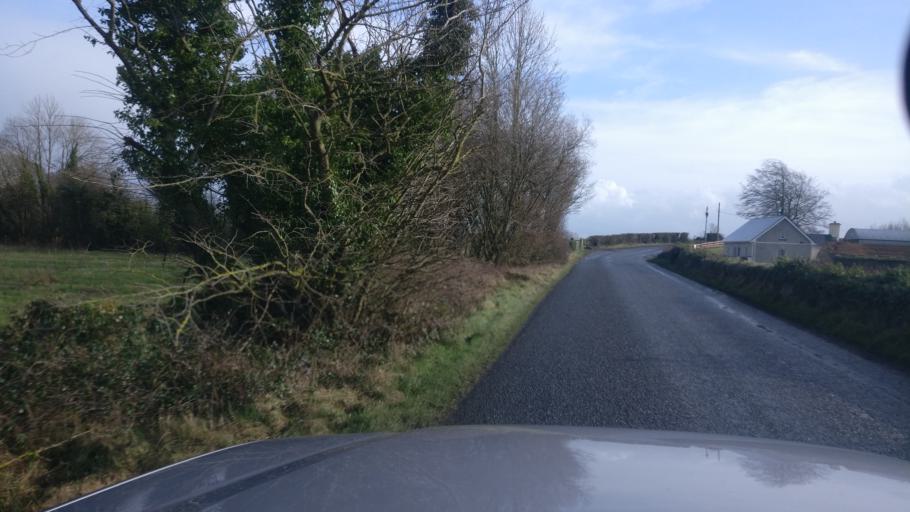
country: IE
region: Leinster
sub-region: Uibh Fhaili
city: Birr
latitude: 52.9773
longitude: -7.9365
